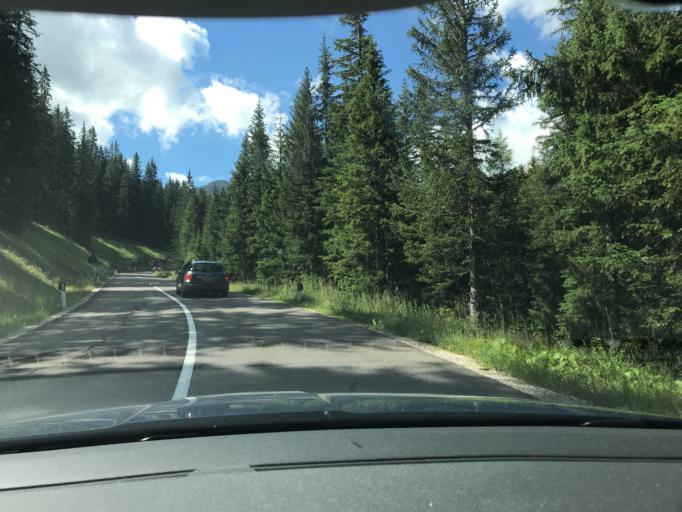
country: IT
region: Veneto
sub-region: Provincia di Belluno
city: Livinallongo del Col di Lana
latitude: 46.5508
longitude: 11.9676
